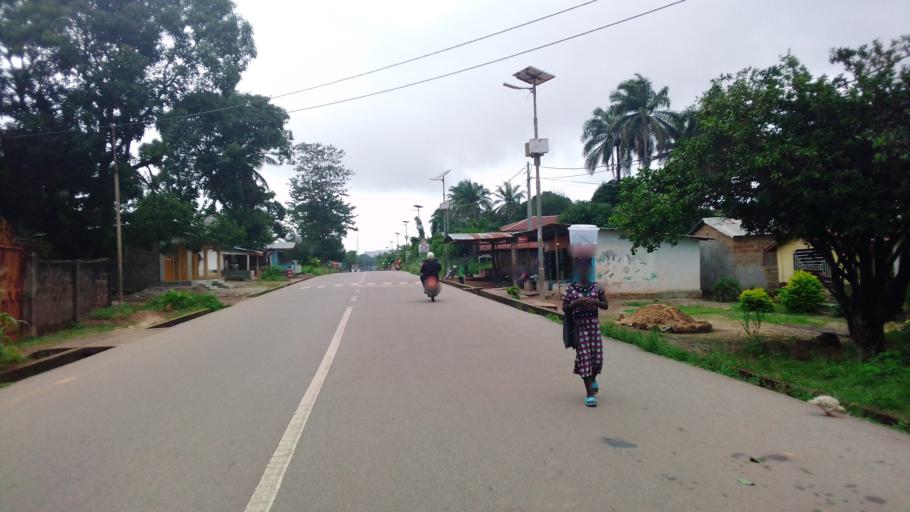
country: SL
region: Northern Province
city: Lunsar
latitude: 8.6871
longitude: -12.5409
